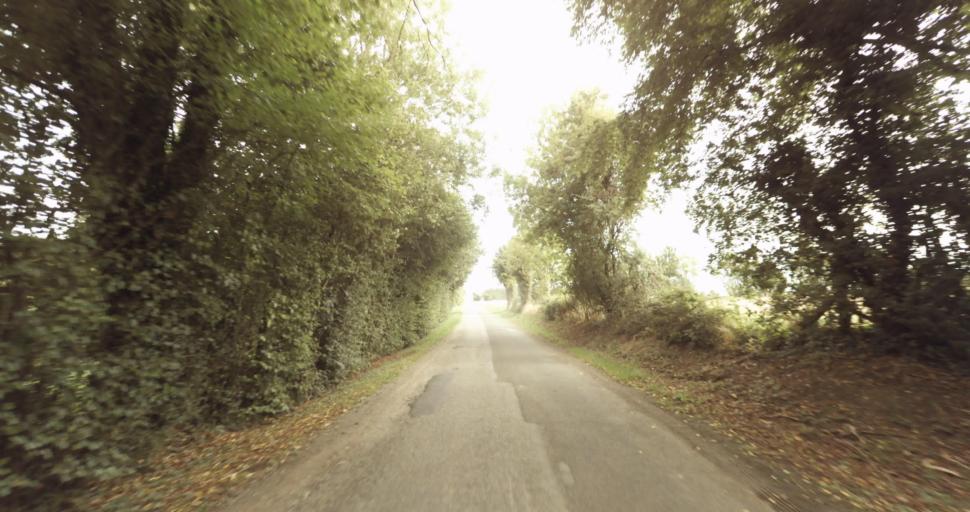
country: FR
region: Lower Normandy
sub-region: Departement de l'Orne
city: Sainte-Gauburge-Sainte-Colombe
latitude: 48.7406
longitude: 0.3664
